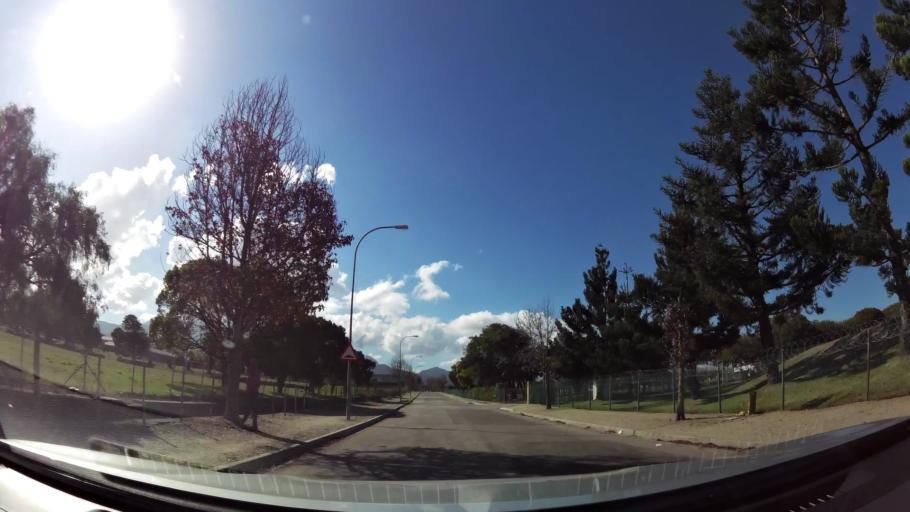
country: ZA
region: Western Cape
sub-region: Eden District Municipality
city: George
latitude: -33.9767
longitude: 22.4470
